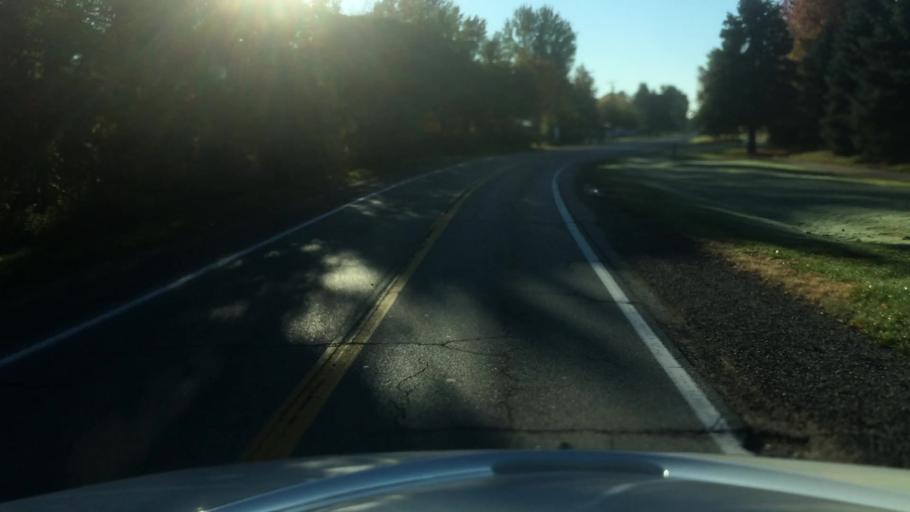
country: US
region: Michigan
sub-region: Macomb County
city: Shelby
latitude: 42.6818
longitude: -82.9476
